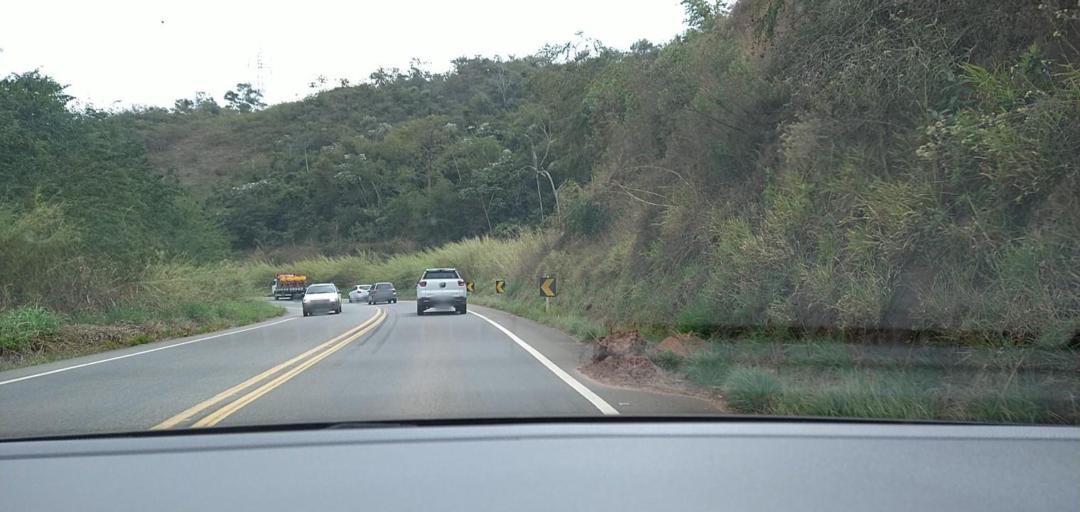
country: BR
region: Minas Gerais
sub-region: Ponte Nova
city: Ponte Nova
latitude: -20.5318
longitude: -42.8927
